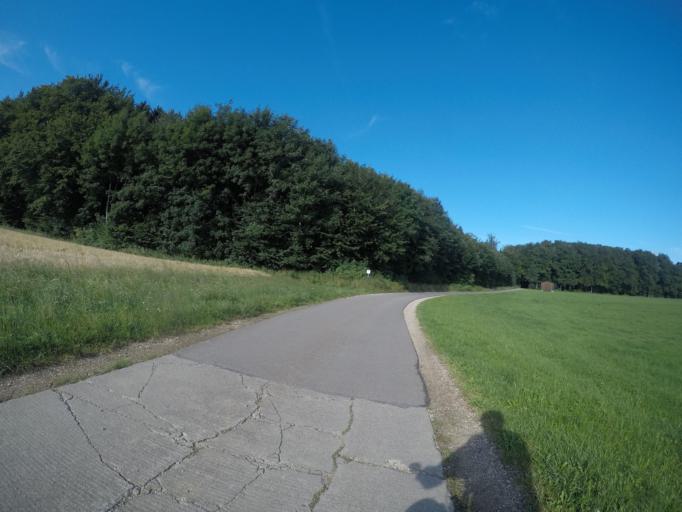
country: DE
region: Baden-Wuerttemberg
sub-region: Tuebingen Region
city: Schelklingen
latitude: 48.3938
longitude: 9.6954
